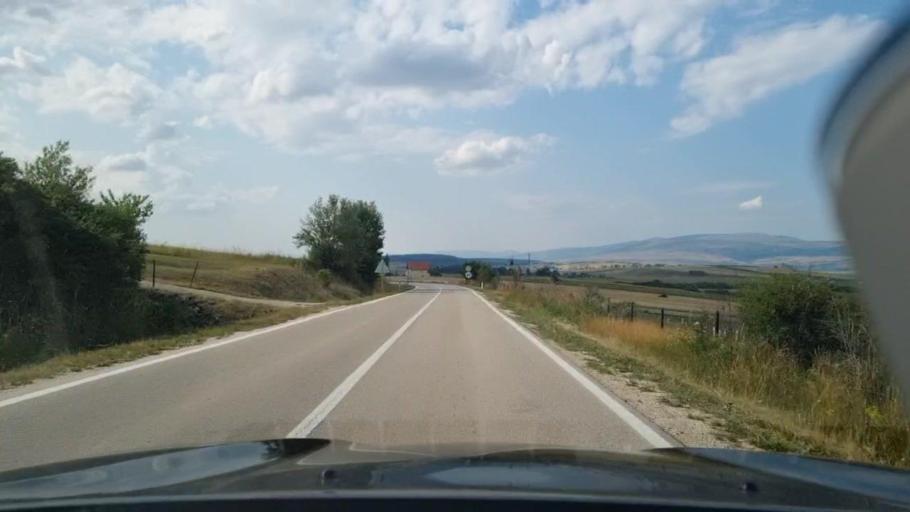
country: BA
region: Federation of Bosnia and Herzegovina
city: Glamoc
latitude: 44.0330
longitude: 16.8828
